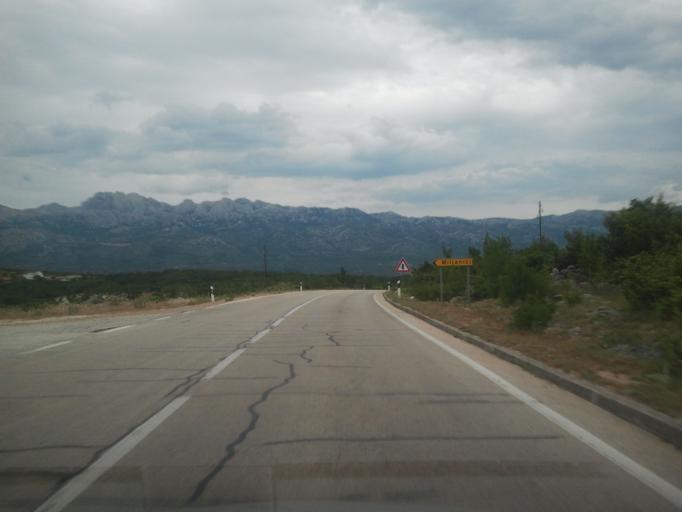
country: HR
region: Zadarska
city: Krusevo
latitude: 44.1890
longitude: 15.6386
